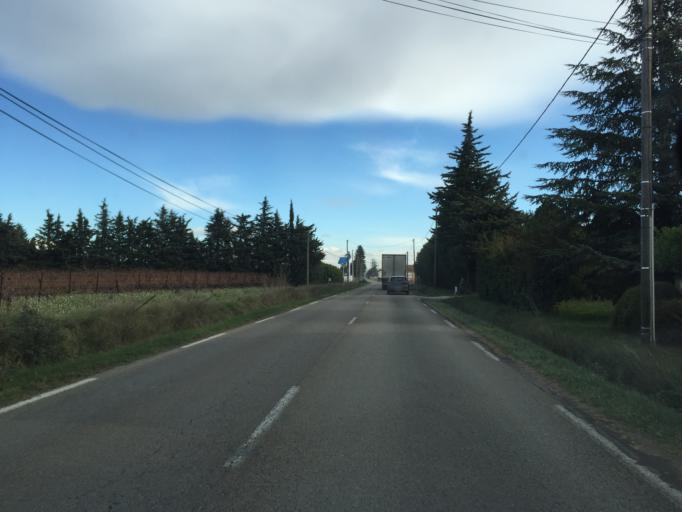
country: FR
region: Provence-Alpes-Cote d'Azur
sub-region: Departement du Vaucluse
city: Maubec
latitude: 43.8688
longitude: 5.1314
